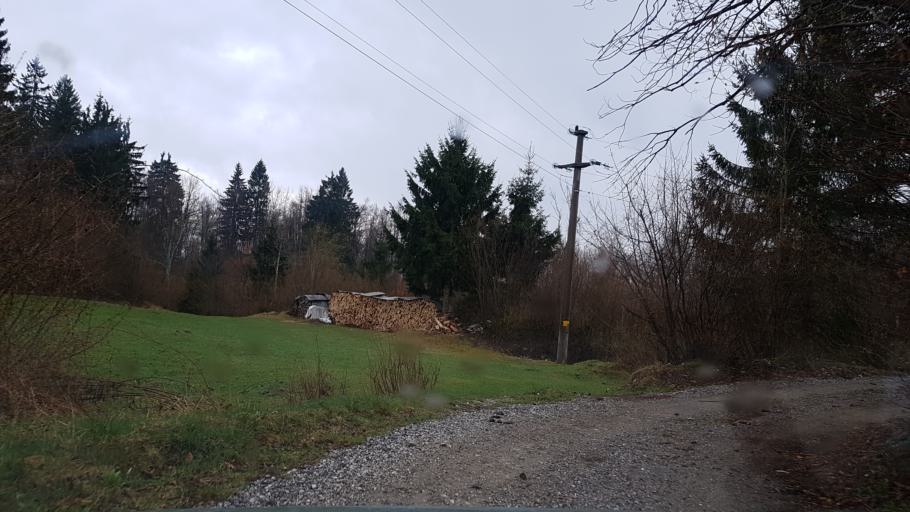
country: SI
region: Cerkno
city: Cerkno
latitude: 46.1411
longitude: 13.8741
